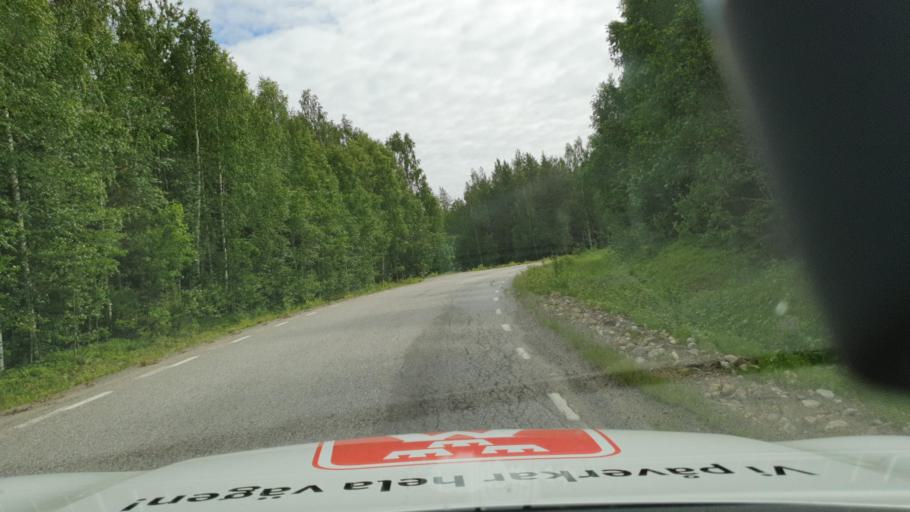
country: SE
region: Vaesterbotten
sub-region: Skelleftea Kommun
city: Burtraesk
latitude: 64.6074
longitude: 20.5626
